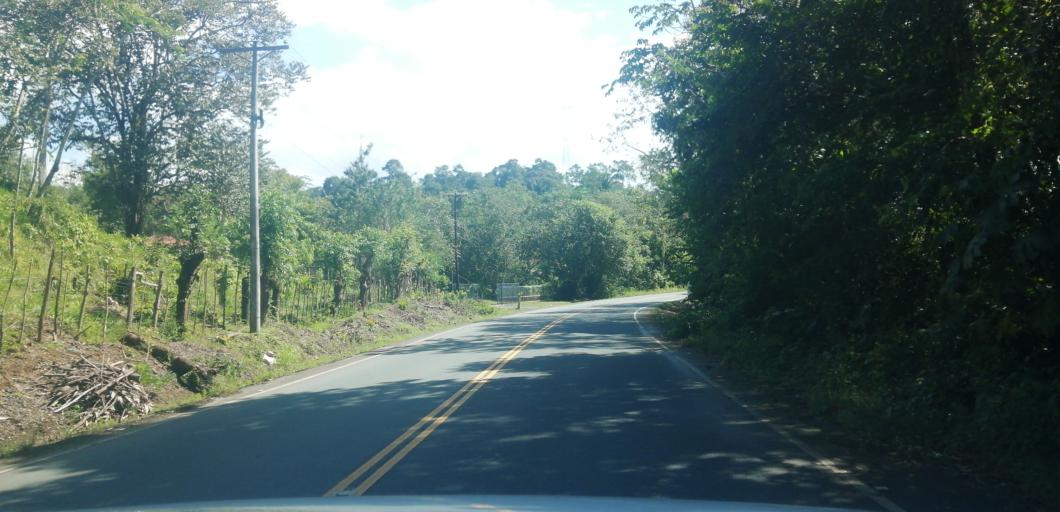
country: PA
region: Panama
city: Canita
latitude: 9.2195
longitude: -78.9324
